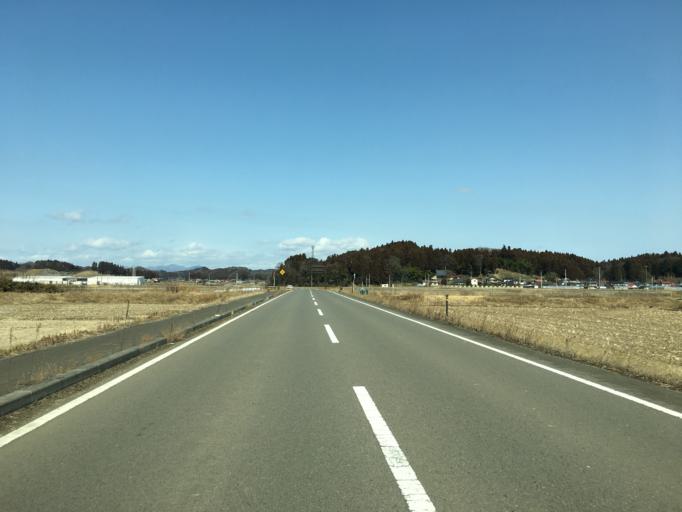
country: JP
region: Fukushima
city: Ishikawa
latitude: 37.1170
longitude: 140.2775
